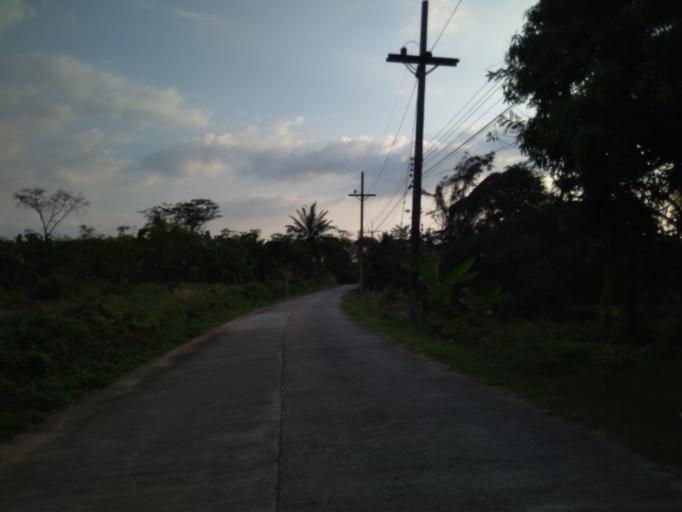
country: TH
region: Phangnga
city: Ko Yao
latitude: 8.1401
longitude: 98.5985
